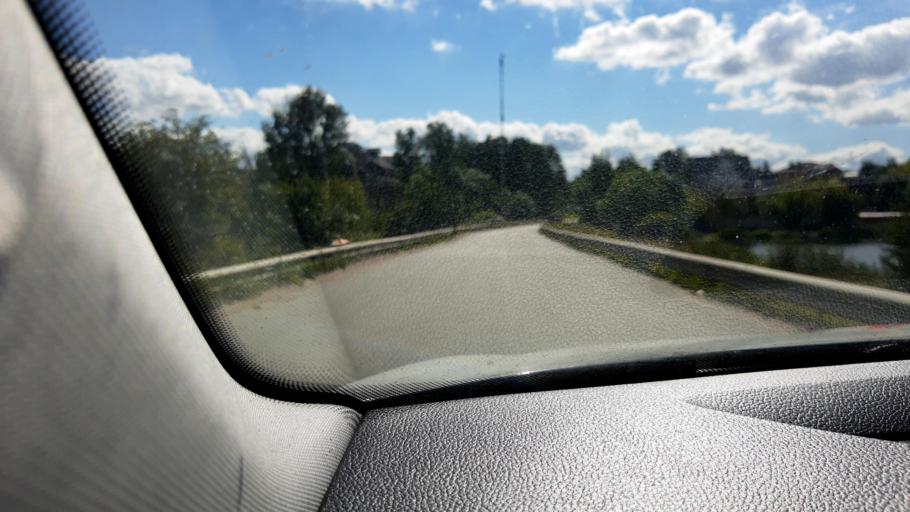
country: RU
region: Moscow
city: Zagor'ye
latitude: 55.5533
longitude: 37.6629
